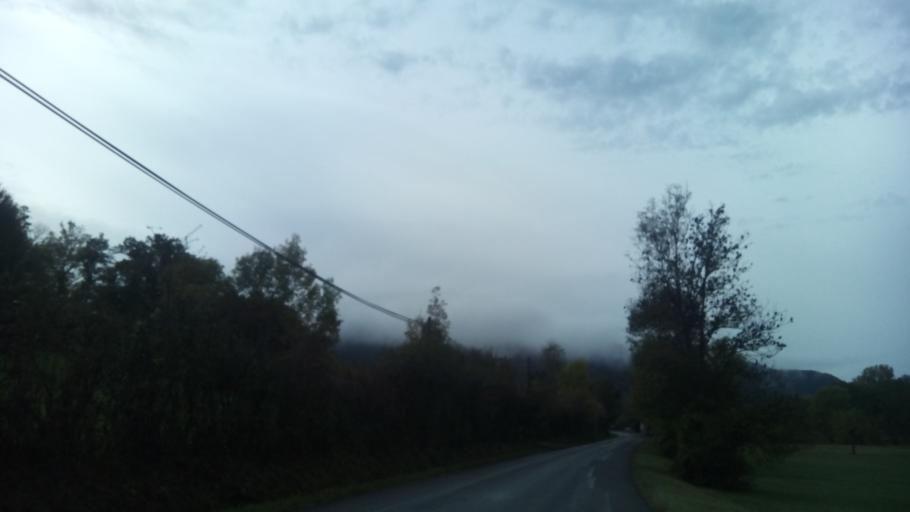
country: FR
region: Midi-Pyrenees
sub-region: Departement du Lot
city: Figeac
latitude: 44.5320
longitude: 1.9748
